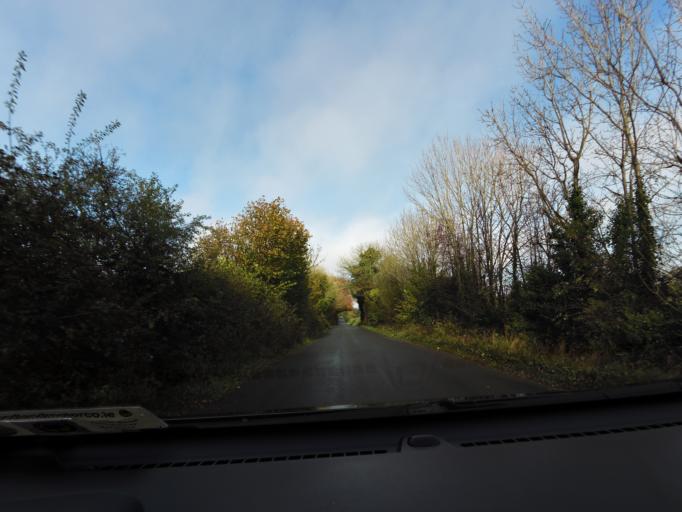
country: IE
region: Leinster
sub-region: An Iarmhi
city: Moate
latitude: 53.3856
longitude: -7.8052
